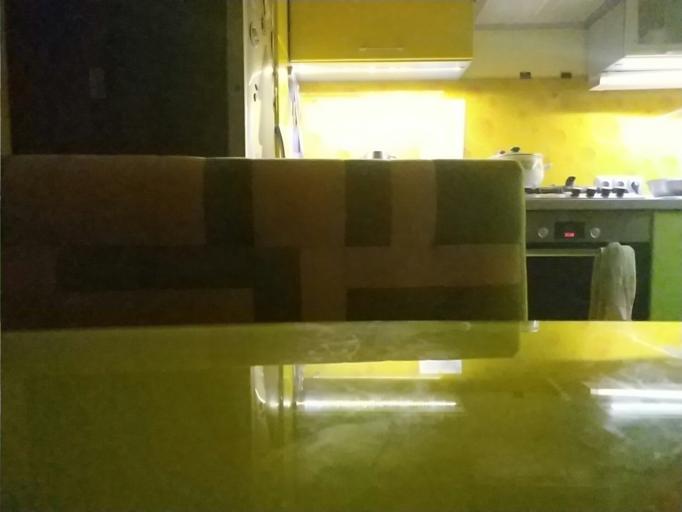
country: RU
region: Republic of Karelia
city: Kalevala
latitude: 65.2693
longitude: 30.7155
